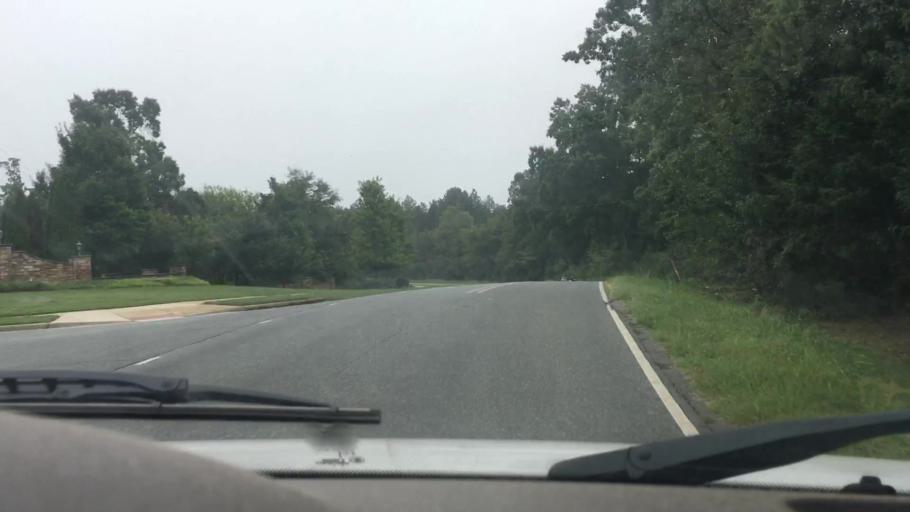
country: US
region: North Carolina
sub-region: Mecklenburg County
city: Huntersville
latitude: 35.3975
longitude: -80.7544
